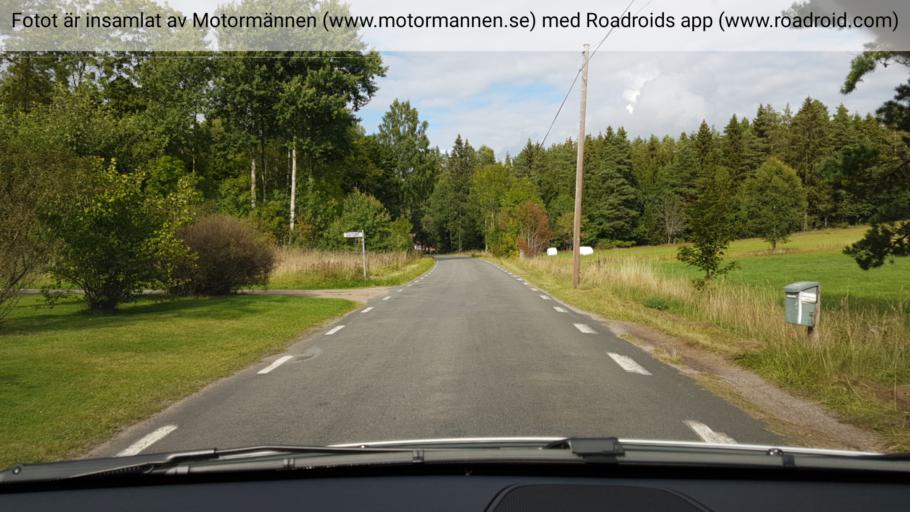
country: SE
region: Vaestra Goetaland
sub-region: Skovde Kommun
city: Skultorp
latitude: 58.2946
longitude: 13.8315
